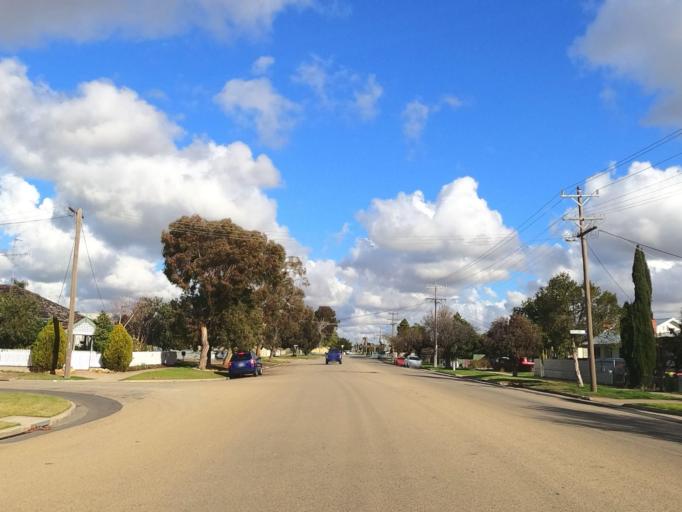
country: AU
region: Victoria
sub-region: Swan Hill
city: Swan Hill
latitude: -35.3312
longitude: 143.5527
